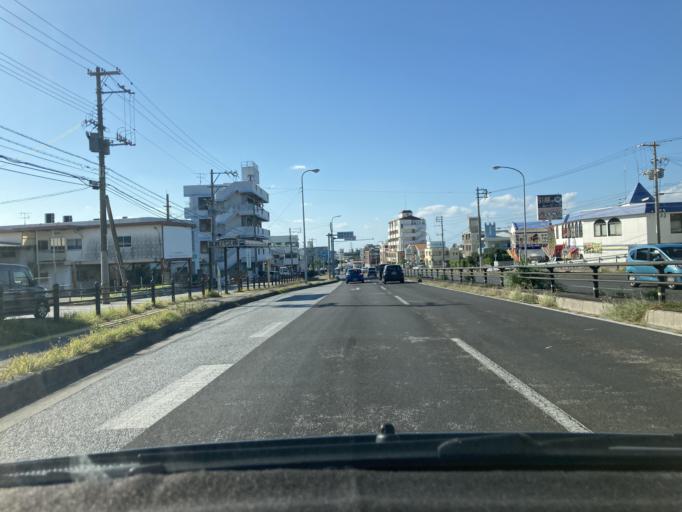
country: JP
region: Okinawa
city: Ginowan
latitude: 26.2550
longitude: 127.7334
